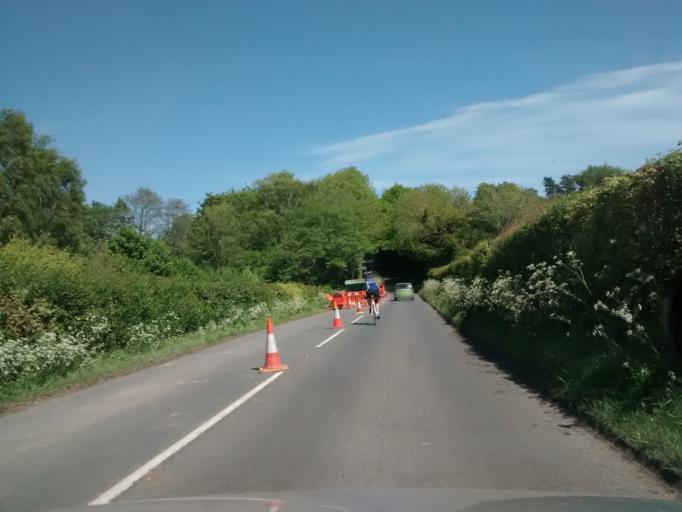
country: GB
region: England
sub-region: Bath and North East Somerset
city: Stanton Drew
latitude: 51.3376
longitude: -2.5858
